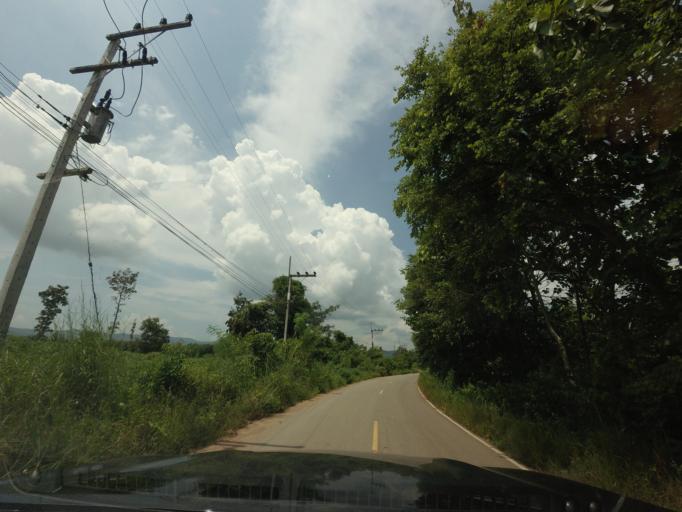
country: TH
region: Khon Kaen
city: Wiang Kao
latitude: 16.6799
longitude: 102.2731
